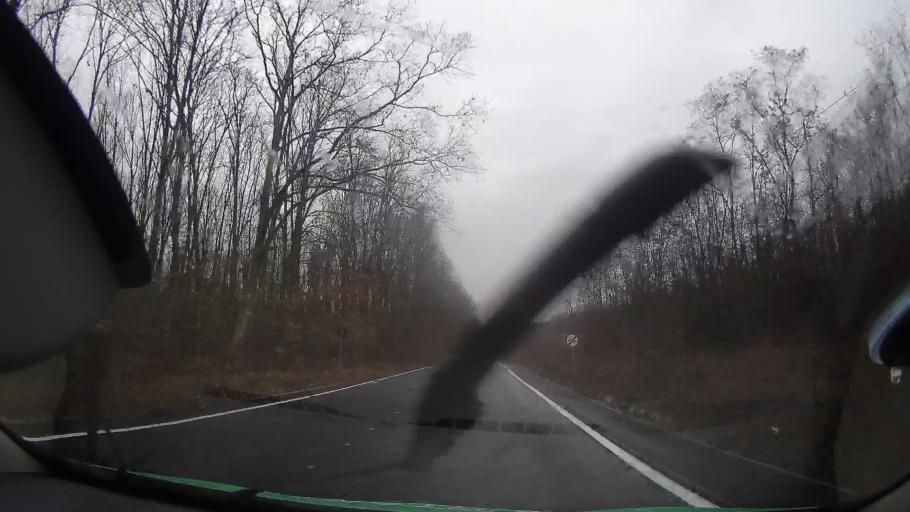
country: RO
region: Bihor
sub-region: Comuna Olcea
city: Olcea
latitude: 46.6960
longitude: 21.9649
